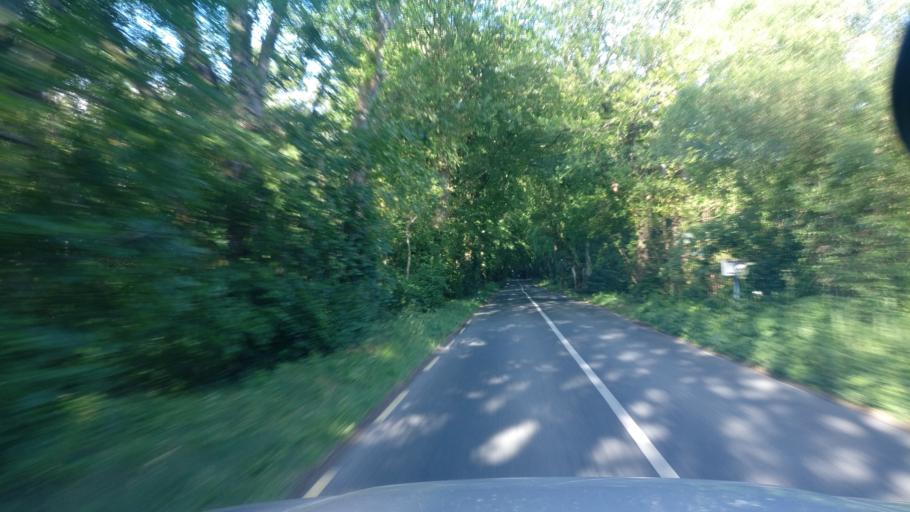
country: IE
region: Connaught
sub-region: County Galway
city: Ballinasloe
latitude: 53.2239
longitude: -8.2137
